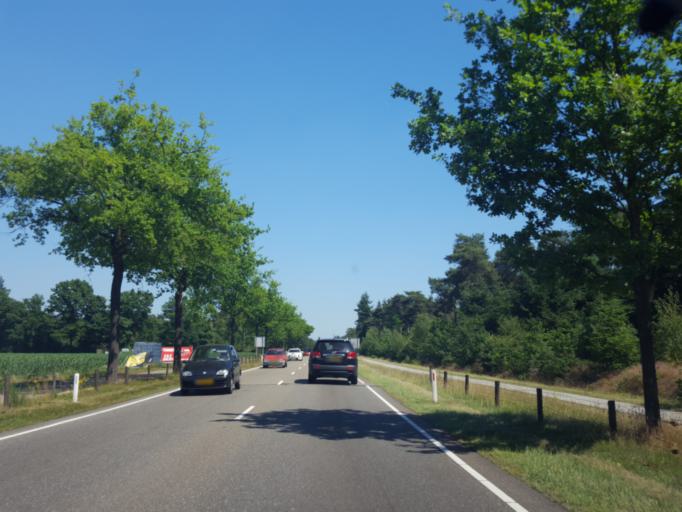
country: NL
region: North Brabant
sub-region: Gemeente Asten
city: Asten
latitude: 51.4687
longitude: 5.7425
